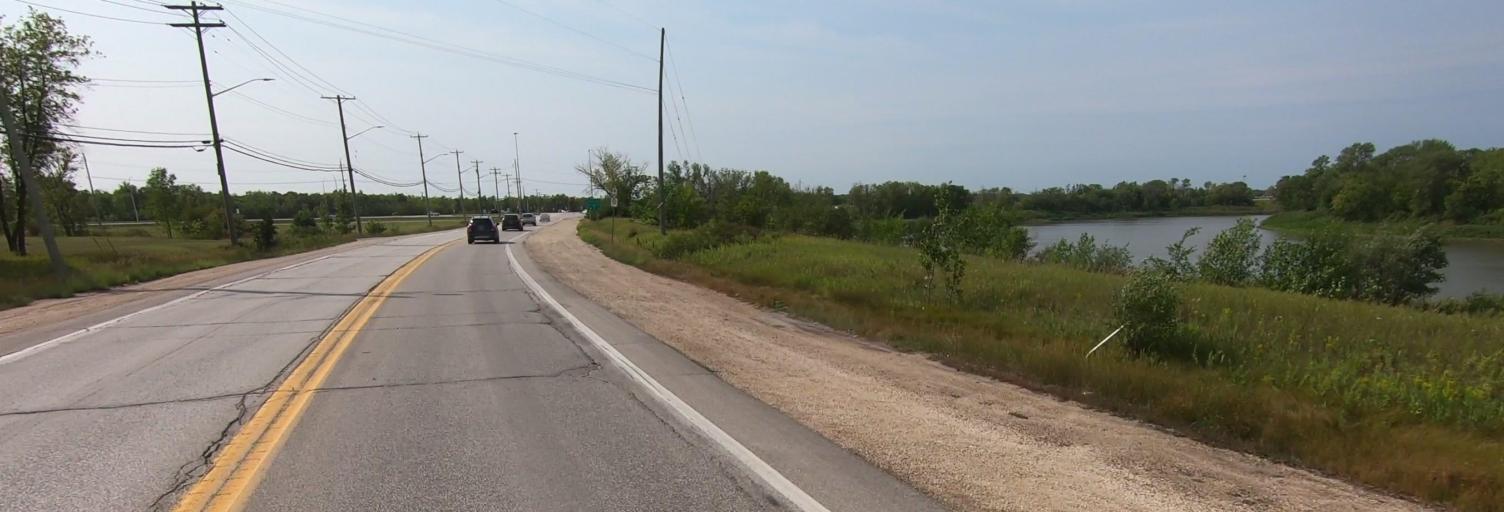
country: CA
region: Manitoba
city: Winnipeg
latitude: 49.7954
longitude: -97.1146
